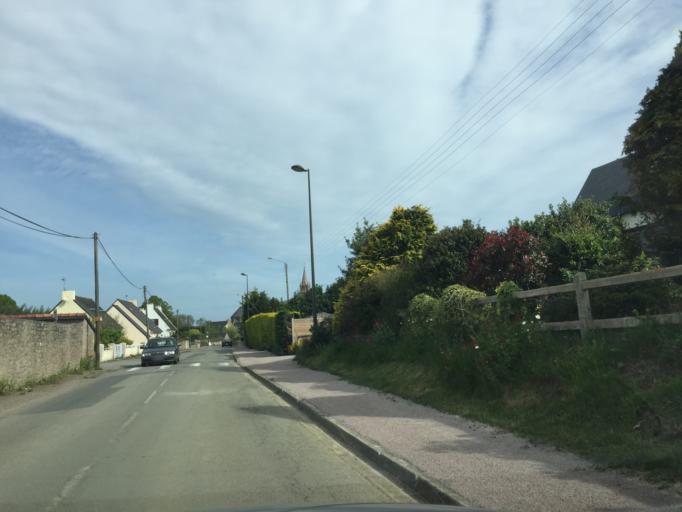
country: FR
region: Brittany
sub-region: Departement des Cotes-d'Armor
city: Matignon
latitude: 48.6522
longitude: -2.3312
